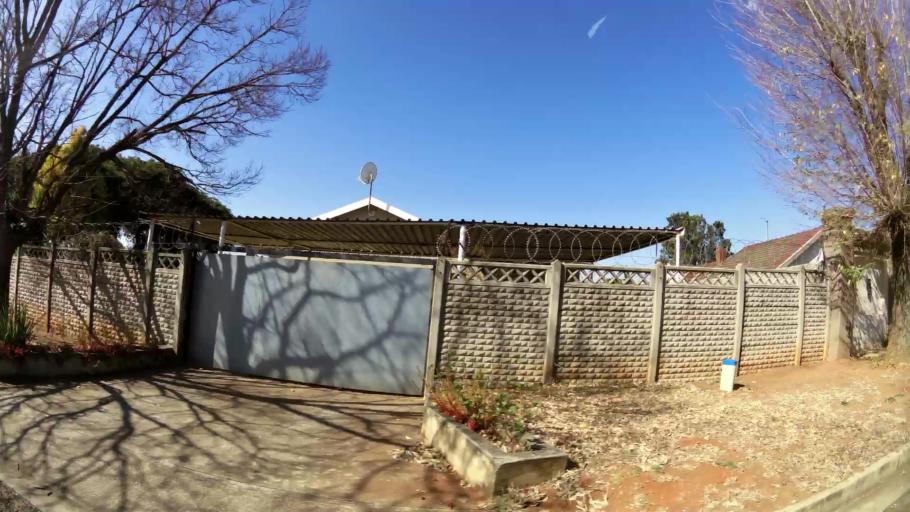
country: ZA
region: Gauteng
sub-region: City of Johannesburg Metropolitan Municipality
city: Modderfontein
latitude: -26.0557
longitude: 28.2074
